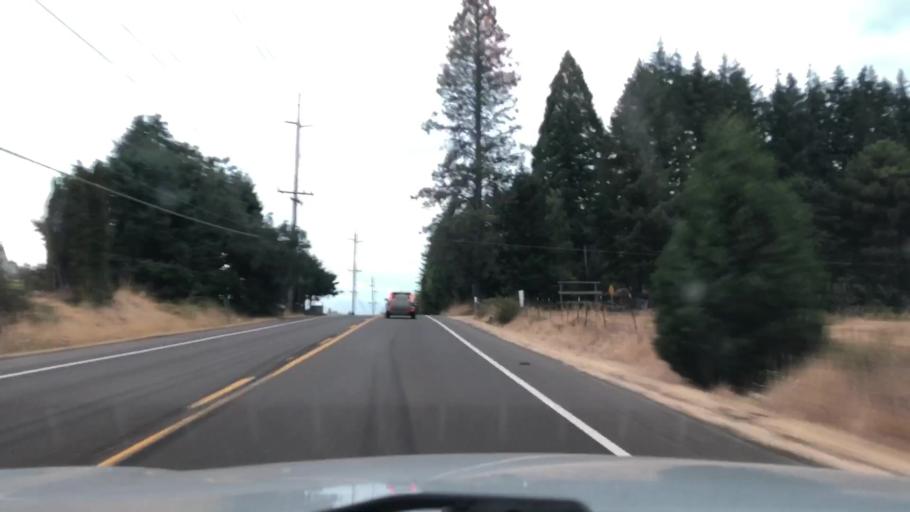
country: US
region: Oregon
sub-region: Clackamas County
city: Beavercreek
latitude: 45.2757
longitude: -122.5688
